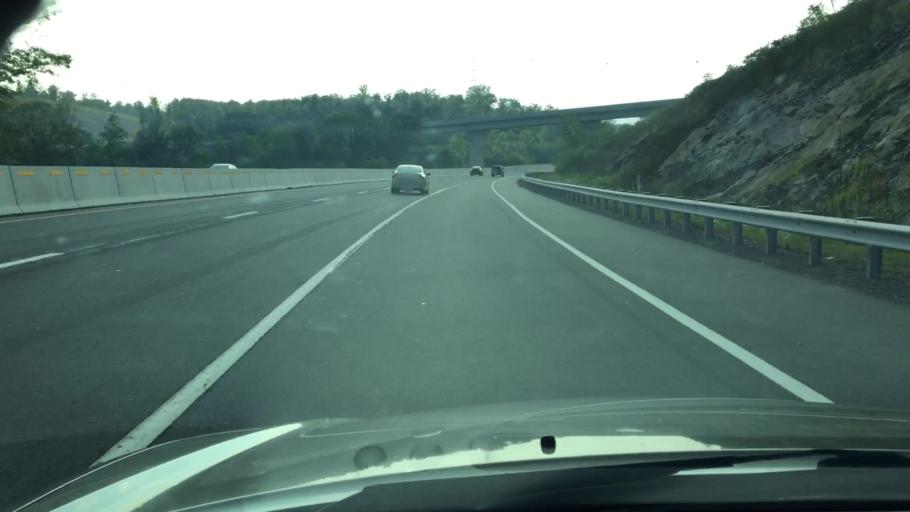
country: US
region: Pennsylvania
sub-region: Luzerne County
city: Nanticoke
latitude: 41.1996
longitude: -75.9616
